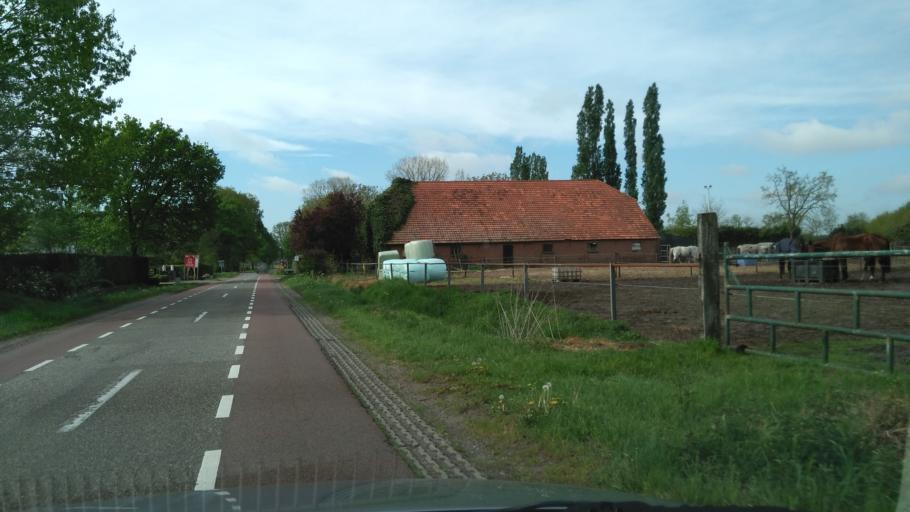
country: BE
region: Flanders
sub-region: Provincie Antwerpen
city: Baarle-Hertog
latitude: 51.4150
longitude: 4.9016
